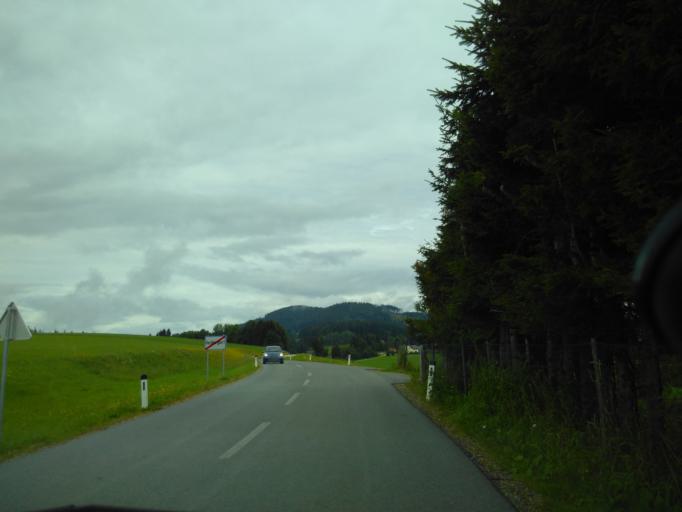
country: AT
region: Styria
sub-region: Politischer Bezirk Graz-Umgebung
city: Semriach
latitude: 47.2636
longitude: 15.4164
